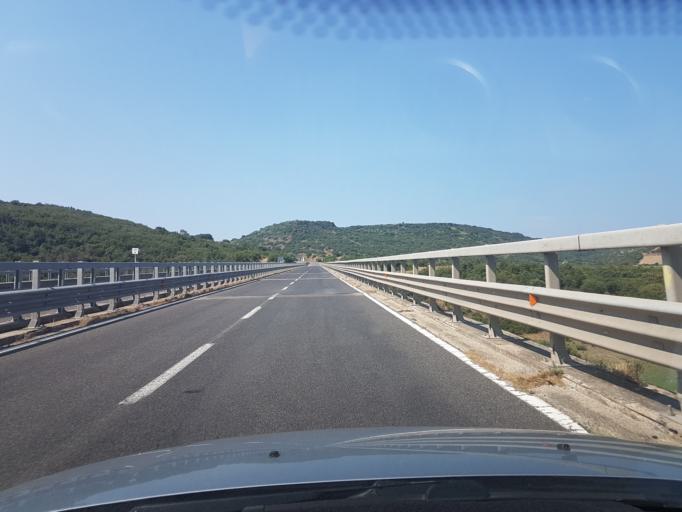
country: IT
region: Sardinia
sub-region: Provincia di Oristano
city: Soddi
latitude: 40.1468
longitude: 8.8796
